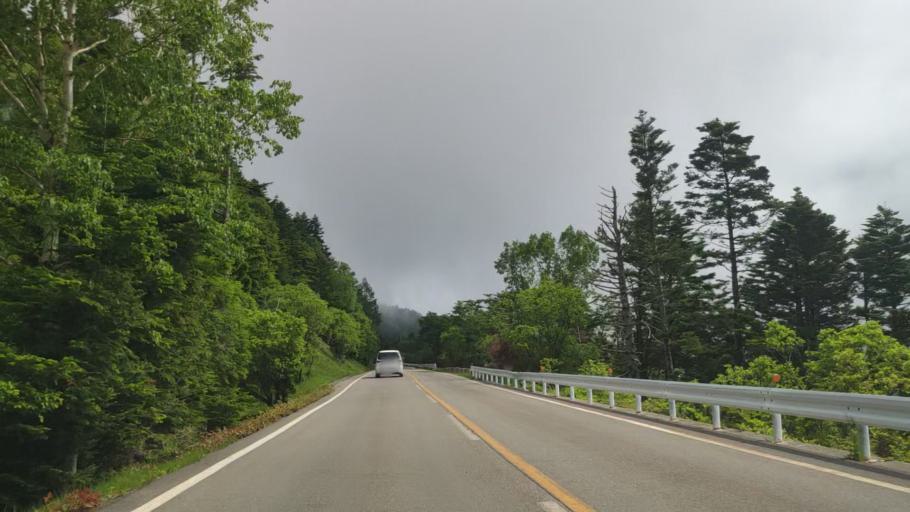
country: JP
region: Yamanashi
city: Fujikawaguchiko
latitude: 35.3979
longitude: 138.6921
